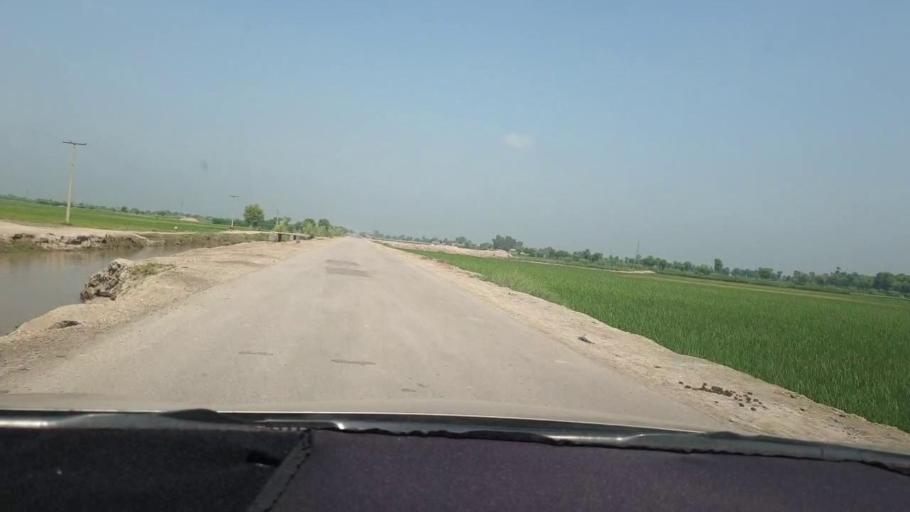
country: PK
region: Sindh
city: Miro Khan
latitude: 27.7738
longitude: 68.0583
